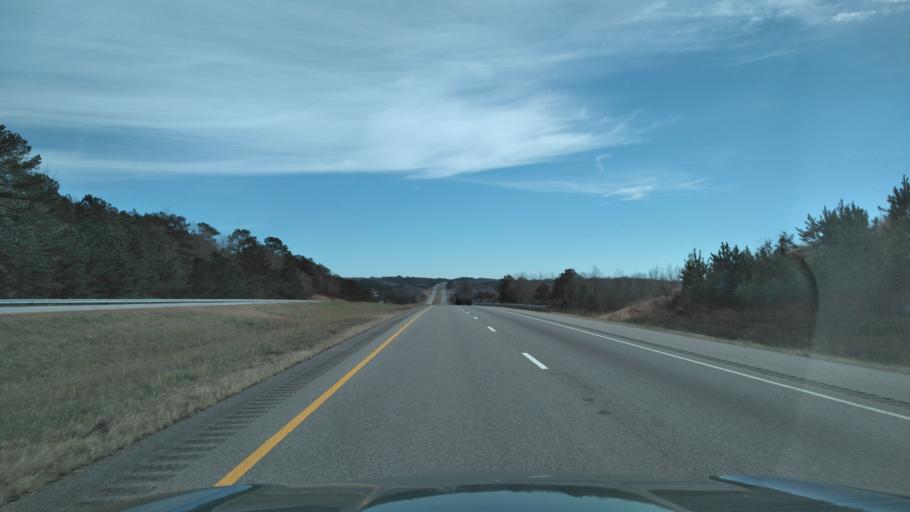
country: US
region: Alabama
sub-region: Marion County
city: Hamilton
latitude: 34.1991
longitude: -88.1450
